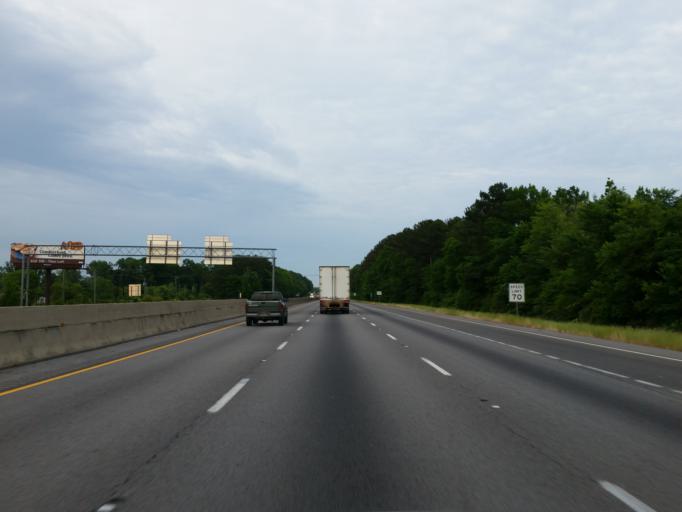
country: US
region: Alabama
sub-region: Jefferson County
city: Leeds
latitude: 33.5669
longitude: -86.5160
